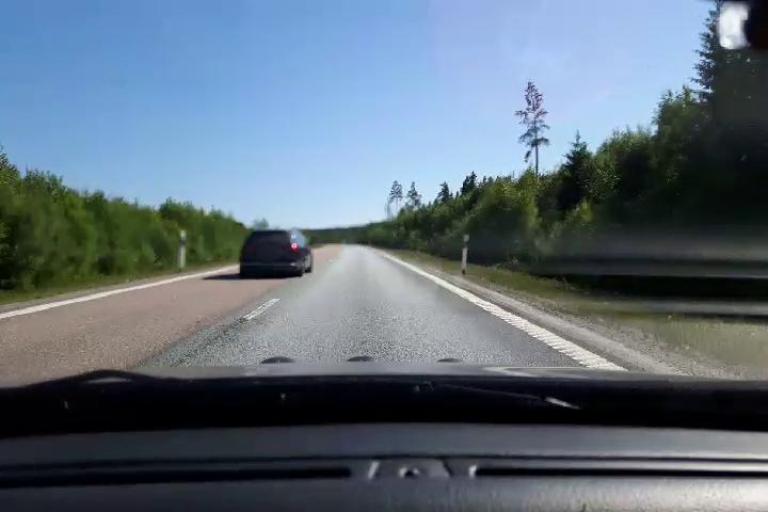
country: SE
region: Gaevleborg
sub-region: Hudiksvalls Kommun
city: Iggesund
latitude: 61.4874
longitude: 16.9838
